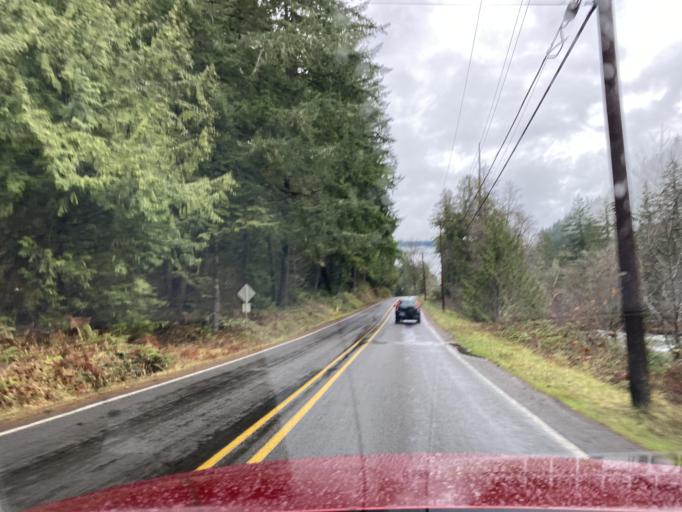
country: US
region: Oregon
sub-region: Lane County
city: Oakridge
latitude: 43.7563
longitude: -122.5085
